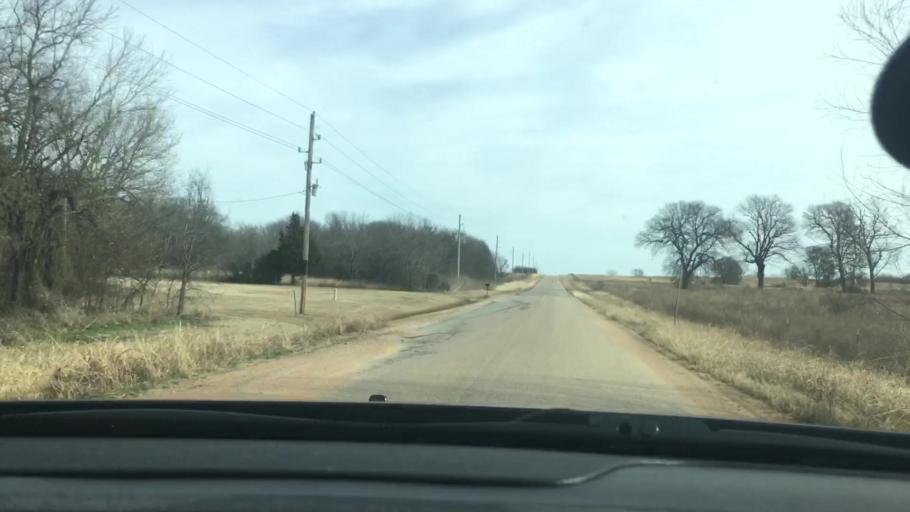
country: US
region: Oklahoma
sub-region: Murray County
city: Sulphur
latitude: 34.4049
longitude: -96.8979
